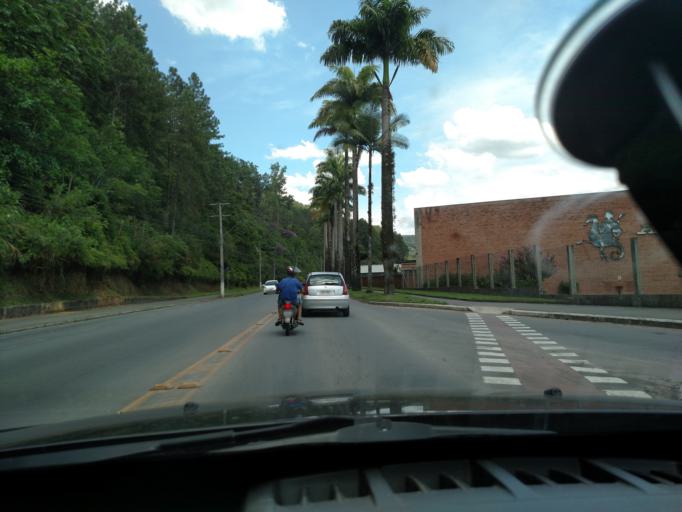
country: BR
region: Santa Catarina
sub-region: Blumenau
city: Blumenau
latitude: -26.9567
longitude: -49.0659
